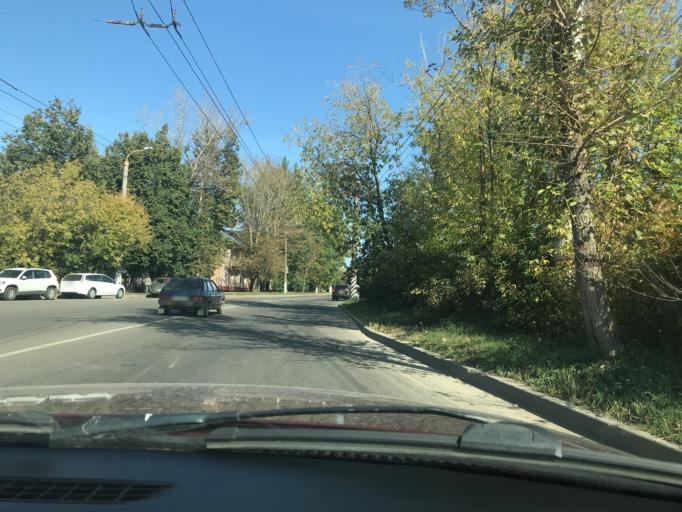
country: RU
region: Kaluga
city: Kaluga
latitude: 54.5373
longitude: 36.2752
